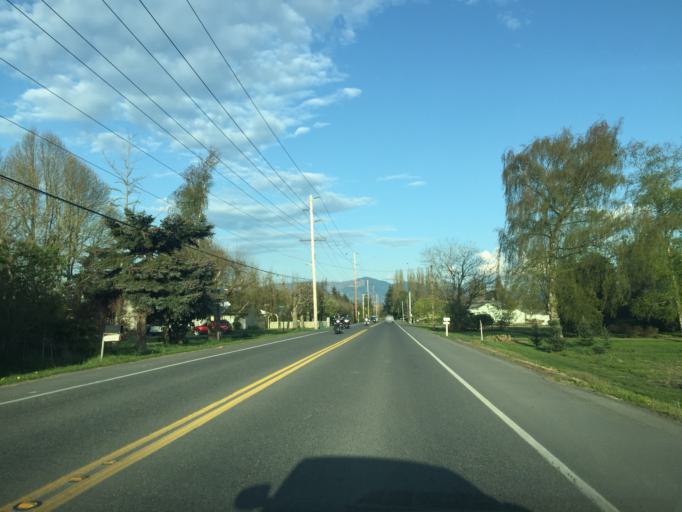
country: US
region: Washington
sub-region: Skagit County
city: Mount Vernon
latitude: 48.4207
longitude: -122.3638
